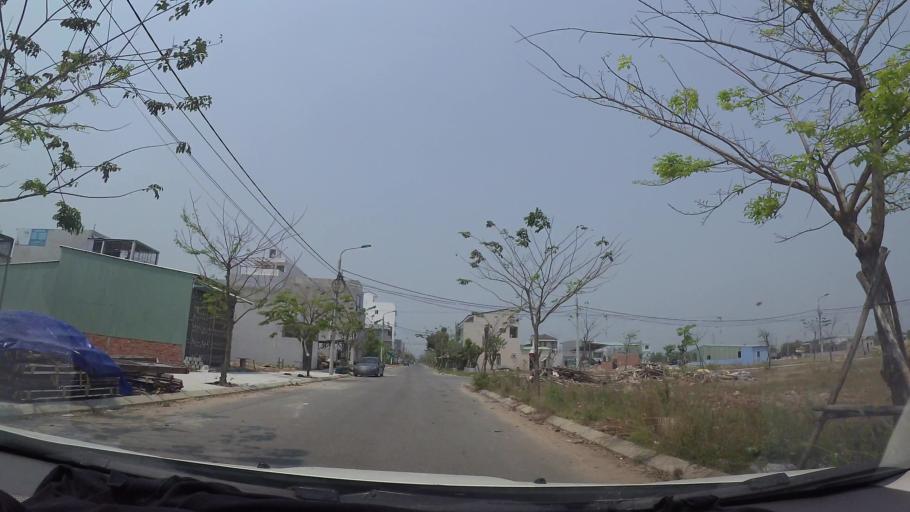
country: VN
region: Da Nang
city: Cam Le
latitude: 16.0146
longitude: 108.2234
